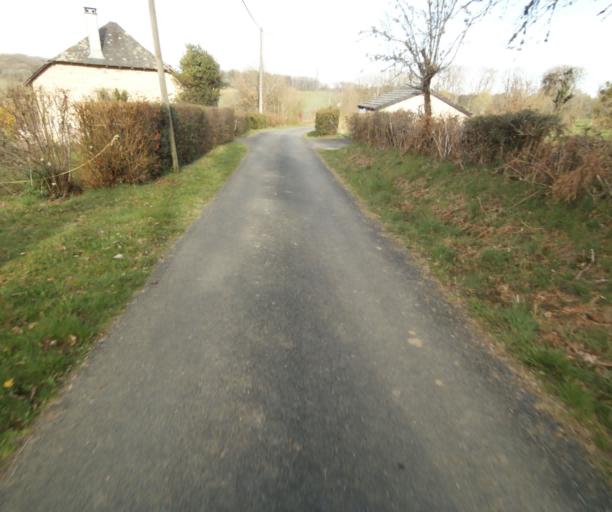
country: FR
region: Limousin
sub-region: Departement de la Correze
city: Chamboulive
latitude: 45.4212
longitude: 1.7625
